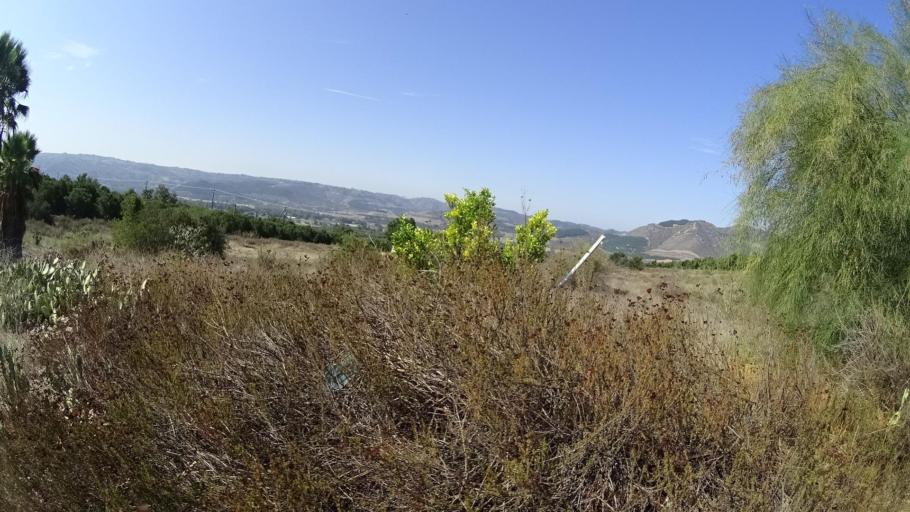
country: US
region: California
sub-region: San Diego County
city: Valley Center
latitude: 33.3371
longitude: -116.9908
